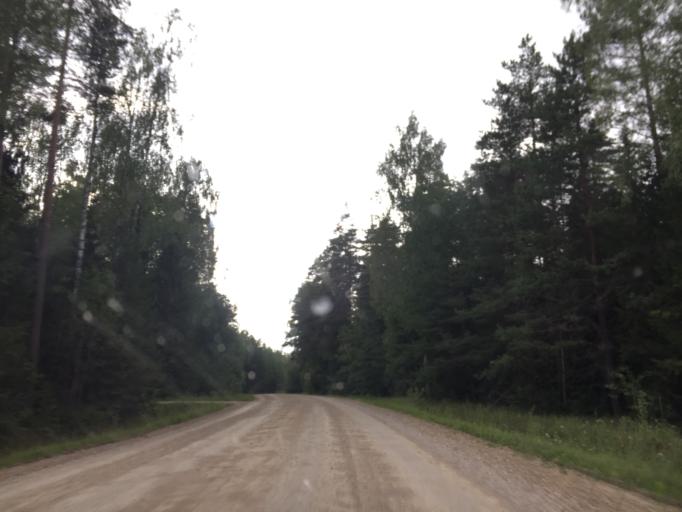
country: LV
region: Sigulda
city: Sigulda
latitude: 57.0835
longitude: 24.8193
